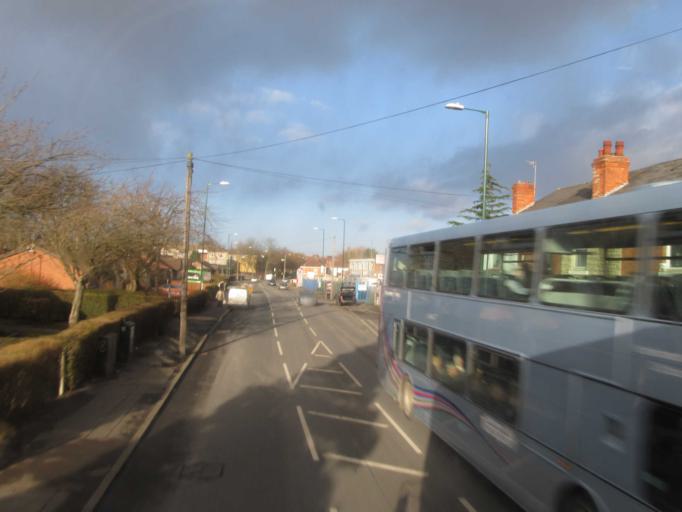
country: GB
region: England
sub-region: Nottinghamshire
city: Hucknall
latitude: 52.9932
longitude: -1.1981
